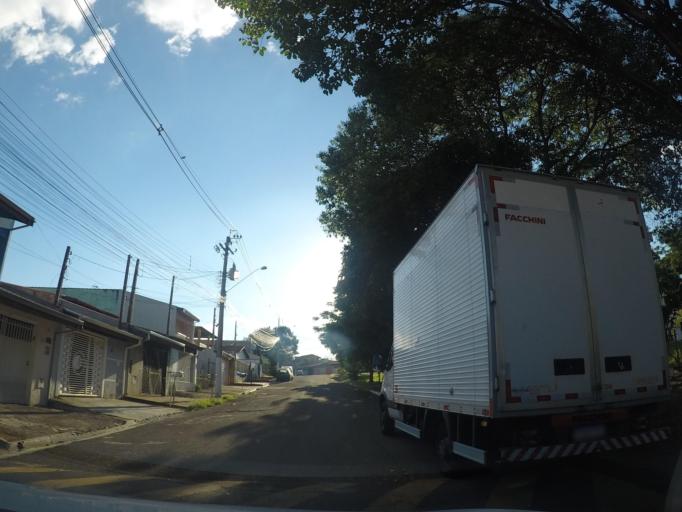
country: BR
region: Sao Paulo
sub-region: Sumare
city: Sumare
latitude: -22.8114
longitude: -47.2395
